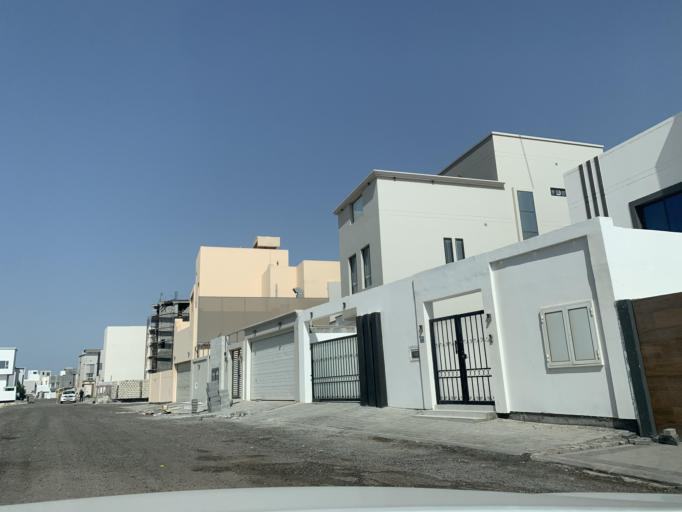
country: BH
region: Manama
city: Jidd Hafs
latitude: 26.2307
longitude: 50.4655
